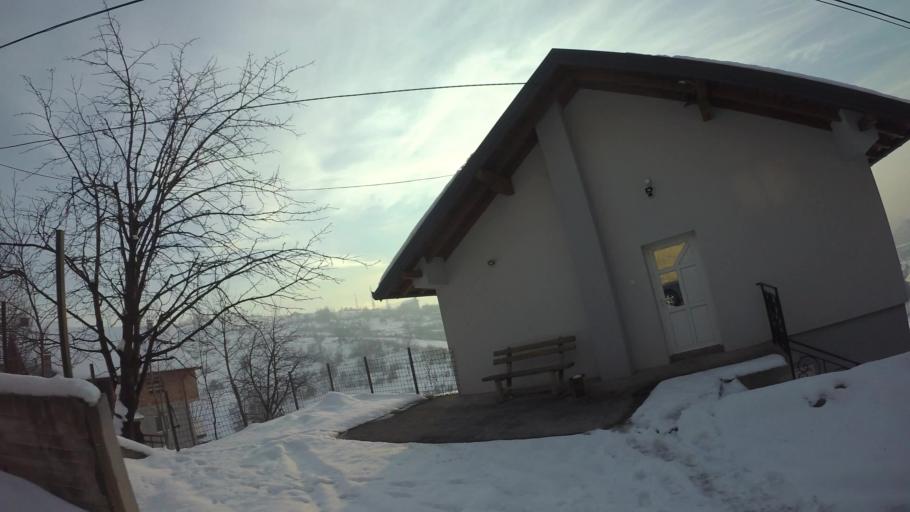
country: BA
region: Federation of Bosnia and Herzegovina
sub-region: Kanton Sarajevo
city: Sarajevo
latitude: 43.8392
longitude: 18.3544
